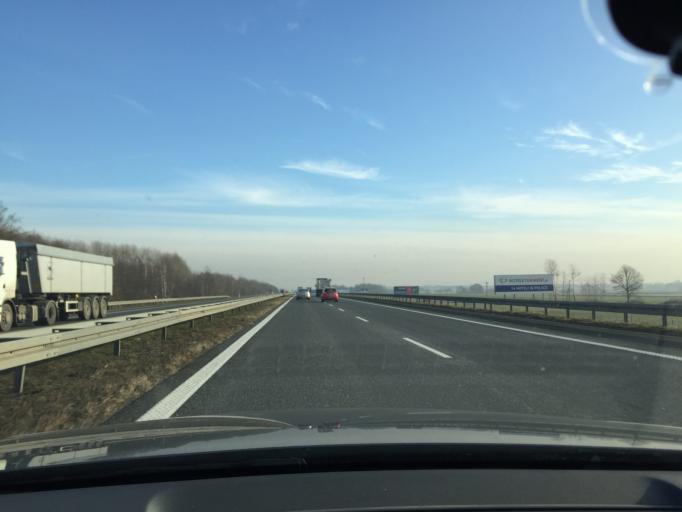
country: PL
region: Silesian Voivodeship
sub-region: Powiat gliwicki
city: Zernica
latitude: 50.2640
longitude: 18.6122
